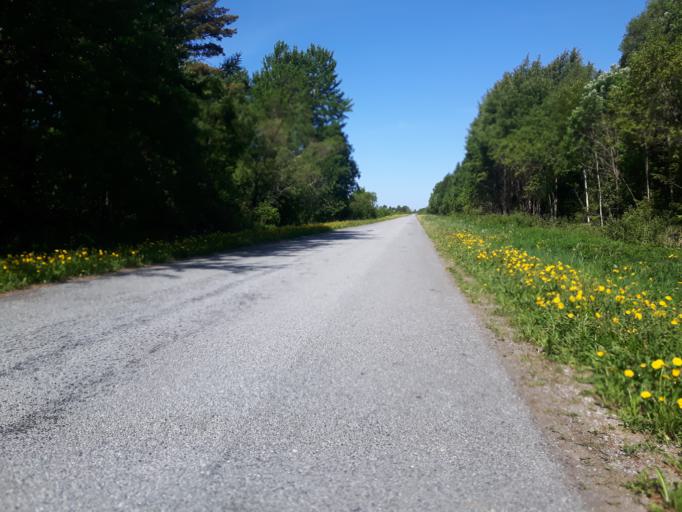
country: EE
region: Ida-Virumaa
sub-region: Aseri vald
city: Aseri
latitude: 59.4580
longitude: 26.8397
